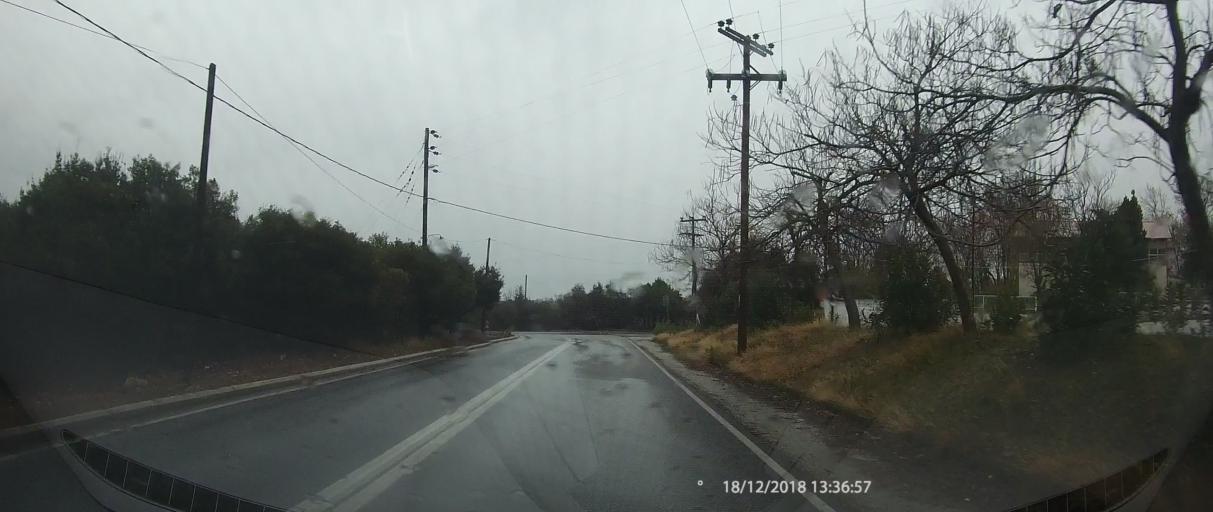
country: GR
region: Central Macedonia
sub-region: Nomos Pierias
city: Litochoro
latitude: 40.1092
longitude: 22.4994
